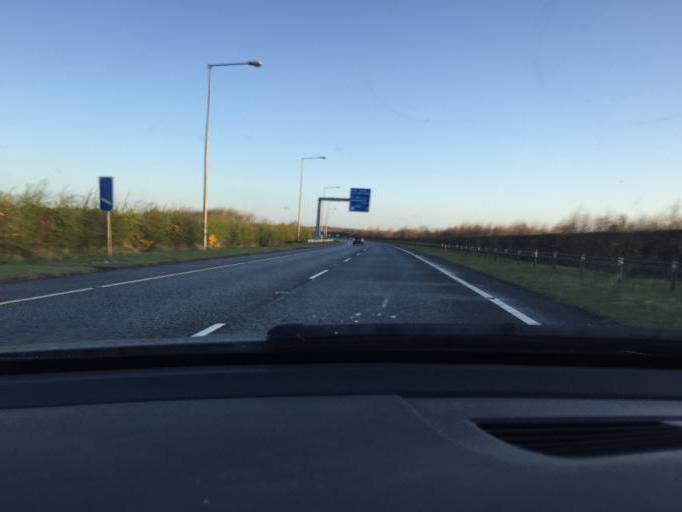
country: IE
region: Leinster
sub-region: An Mhi
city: Stamullin
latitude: 53.6296
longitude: -6.2500
